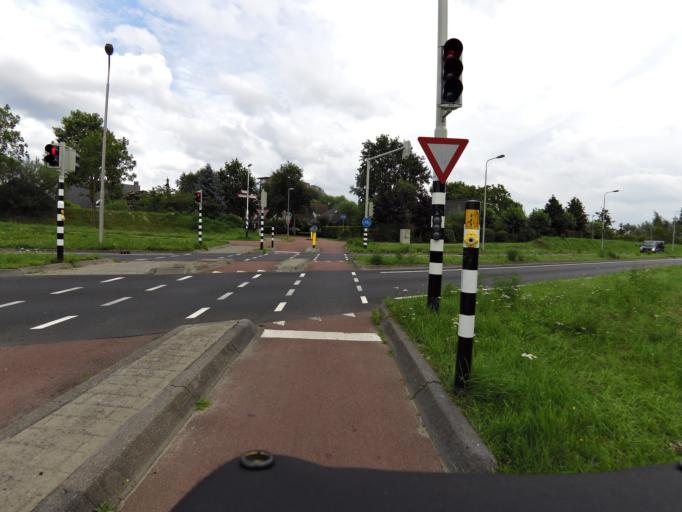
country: NL
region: North Brabant
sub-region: Gemeente Breda
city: Breda
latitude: 51.5868
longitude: 4.7424
